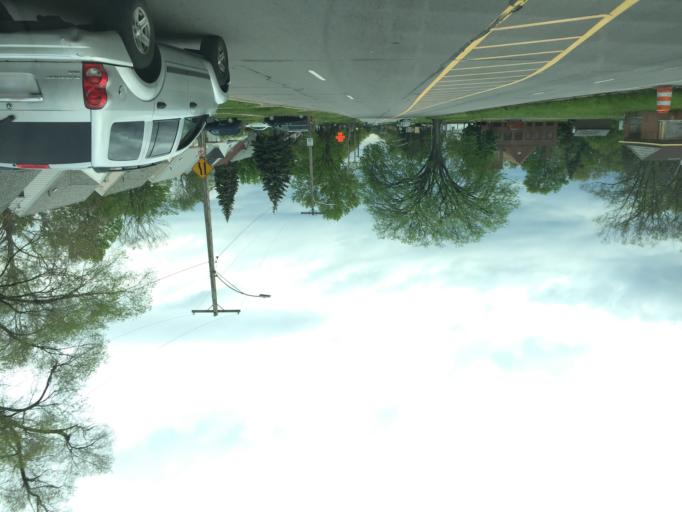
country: US
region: Michigan
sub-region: Wayne County
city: Redford
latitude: 42.3867
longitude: -83.2368
